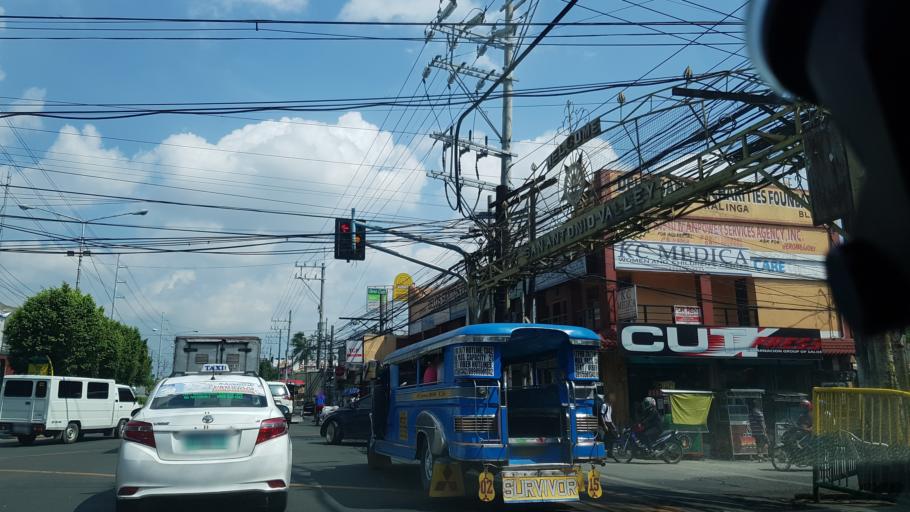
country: PH
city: Sambayanihan People's Village
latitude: 14.4711
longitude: 121.0077
